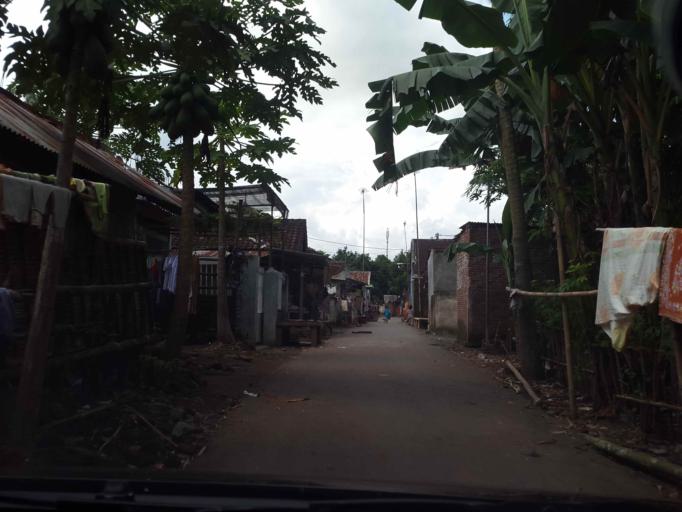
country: ID
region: West Nusa Tenggara
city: Karang Kuripan
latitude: -8.6765
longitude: 116.1663
